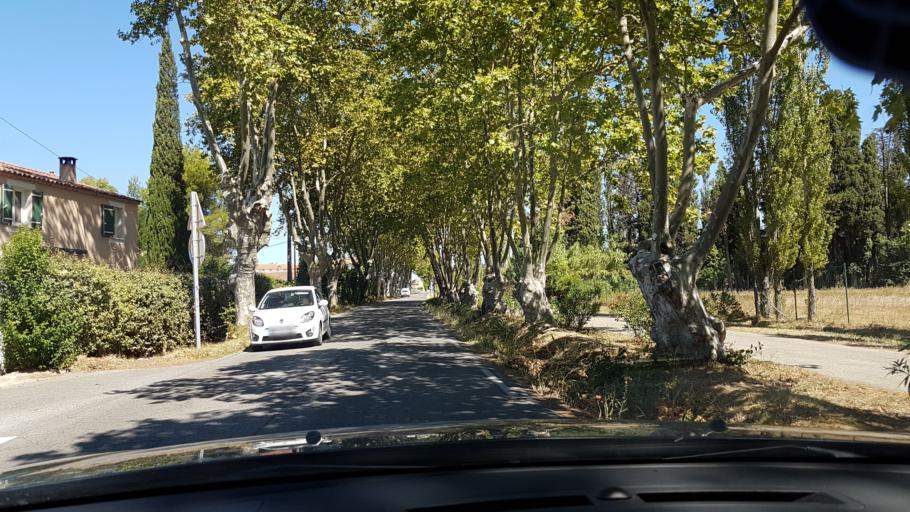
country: FR
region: Provence-Alpes-Cote d'Azur
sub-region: Departement des Bouches-du-Rhone
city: Saint-Andiol
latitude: 43.8273
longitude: 4.9453
